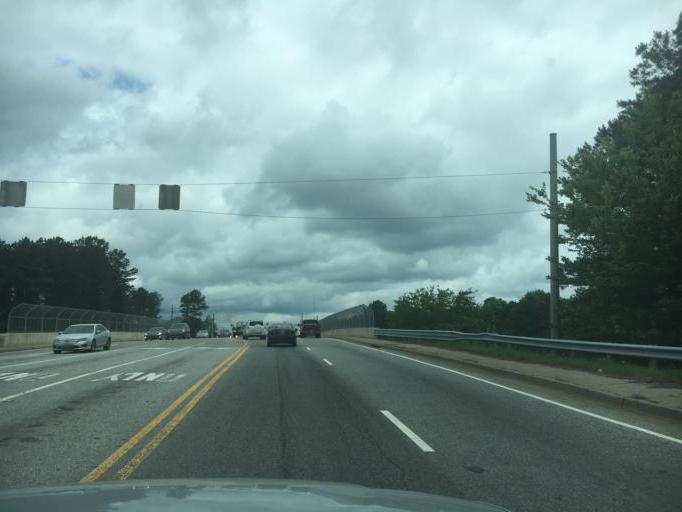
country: US
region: Georgia
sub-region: Gwinnett County
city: Dacula
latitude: 34.0743
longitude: -83.9177
